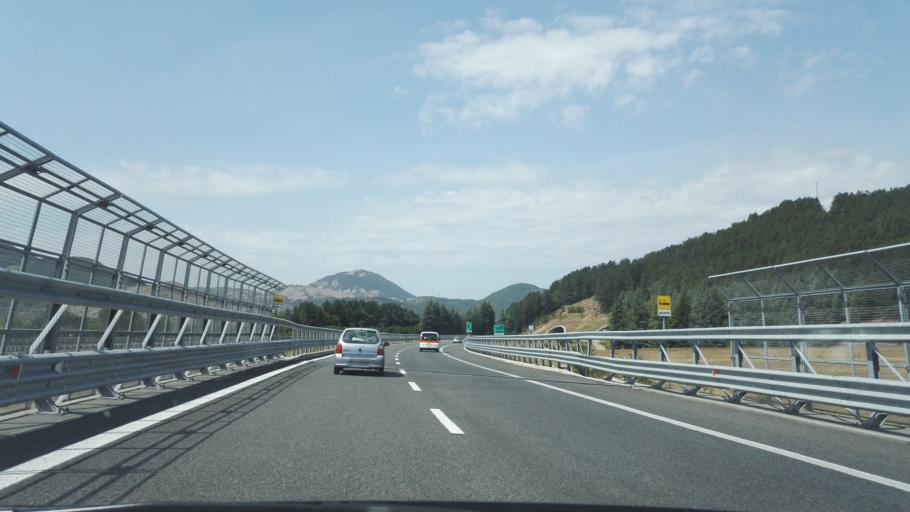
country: IT
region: Calabria
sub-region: Provincia di Cosenza
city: Morano Calabro
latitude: 39.8643
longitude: 16.0890
